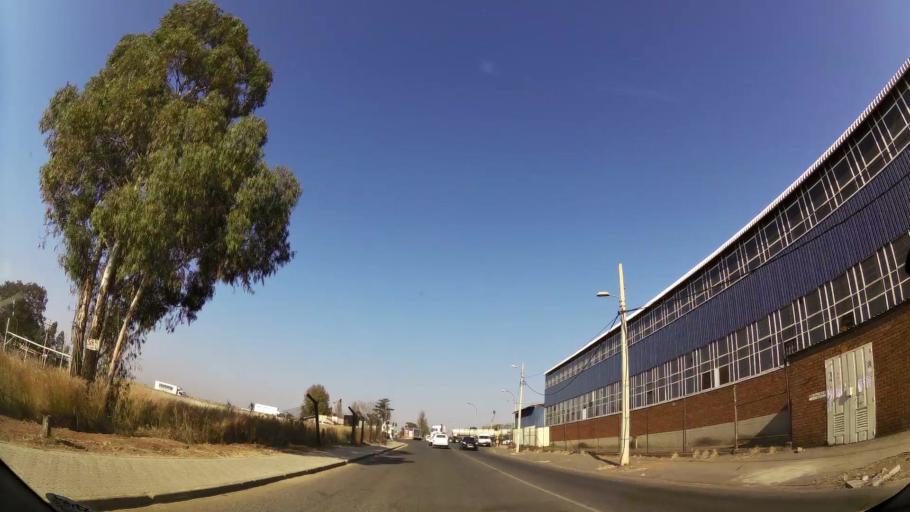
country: ZA
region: Gauteng
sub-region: Ekurhuleni Metropolitan Municipality
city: Germiston
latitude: -26.1715
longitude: 28.2020
